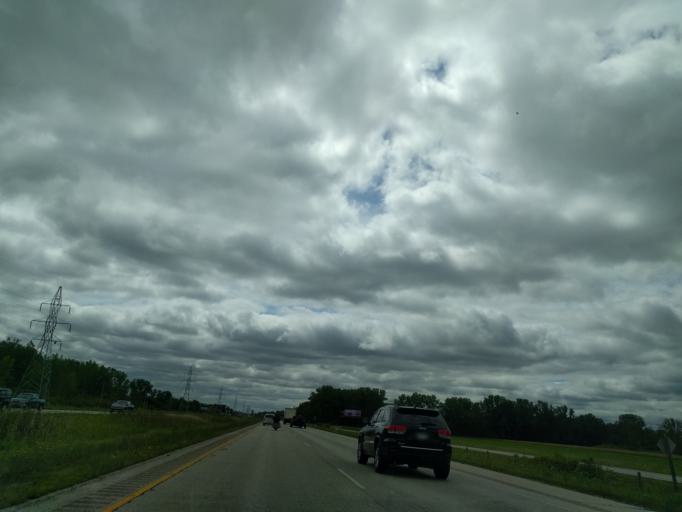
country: US
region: Wisconsin
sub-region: Brown County
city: Suamico
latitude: 44.6161
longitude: -88.0502
